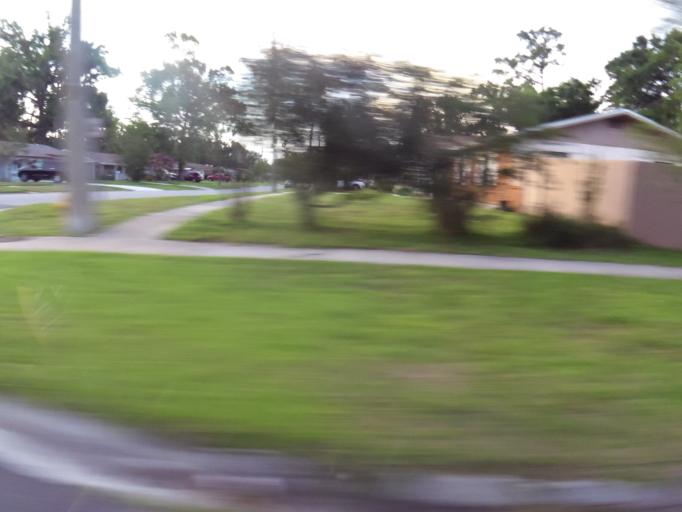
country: US
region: Florida
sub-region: Duval County
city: Jacksonville
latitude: 30.2705
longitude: -81.6043
